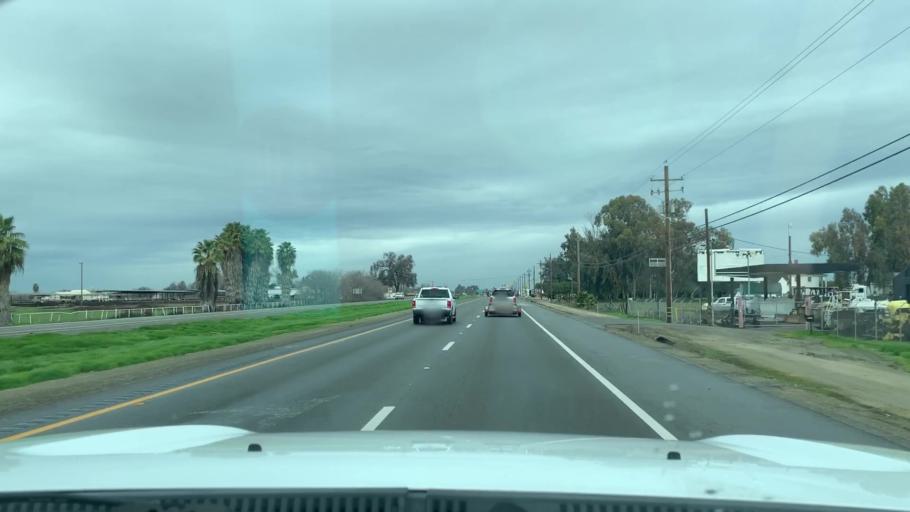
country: US
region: California
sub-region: Kings County
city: Lemoore
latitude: 36.3356
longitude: -119.8079
